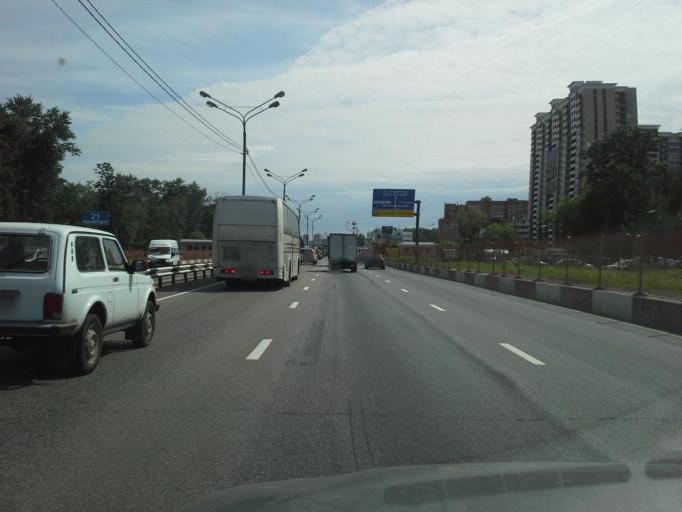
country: RU
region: Moskovskaya
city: Saltykovka
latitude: 55.7938
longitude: 37.9288
